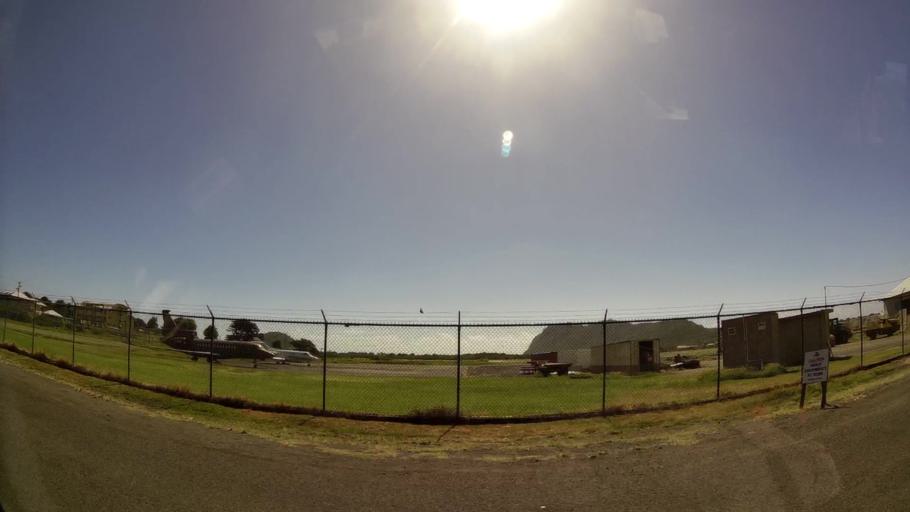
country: LC
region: Vieux-Fort
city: Vieux Fort
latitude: 13.7375
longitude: -60.9467
